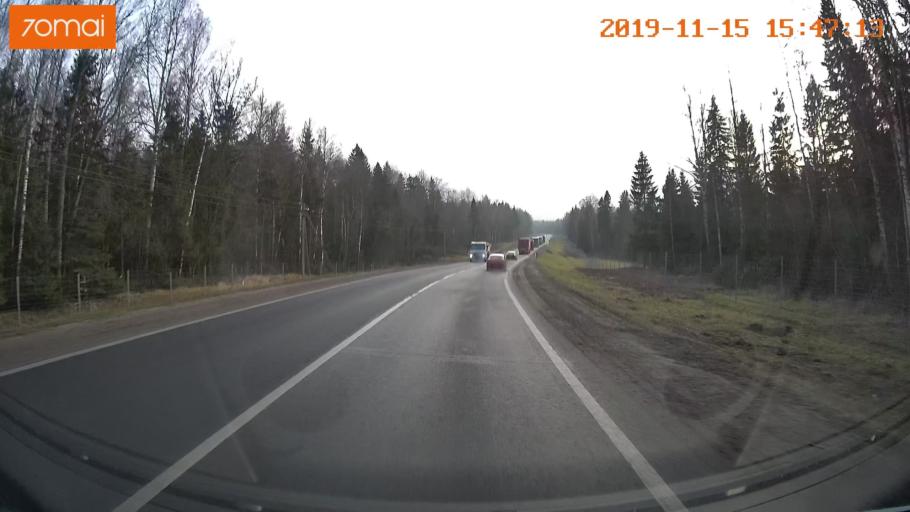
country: RU
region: Jaroslavl
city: Danilov
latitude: 57.9408
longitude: 40.0113
